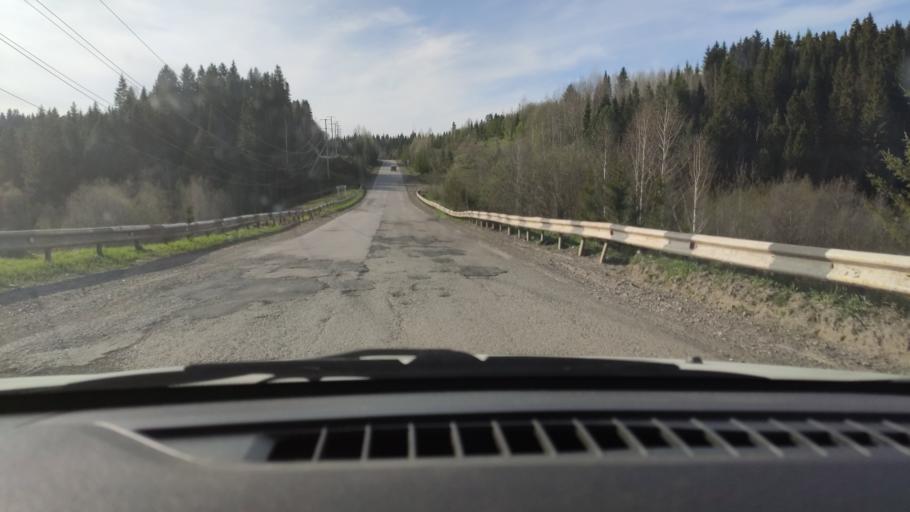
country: RU
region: Perm
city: Novyye Lyady
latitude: 57.9413
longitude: 56.6183
